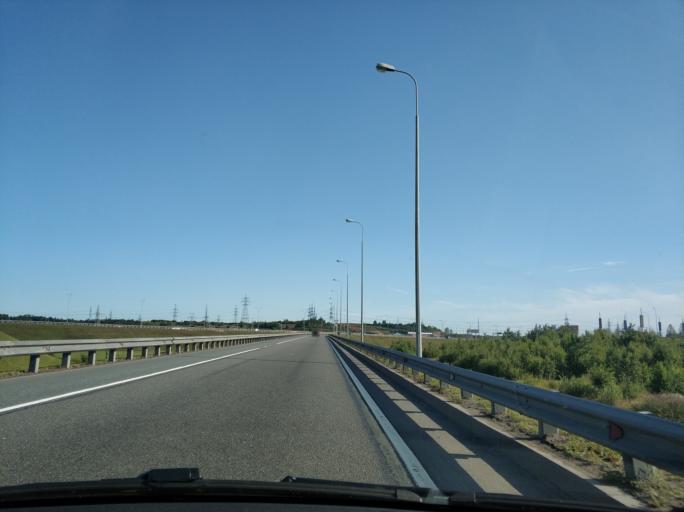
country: RU
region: Leningrad
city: Bugry
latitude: 60.0911
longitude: 30.3726
